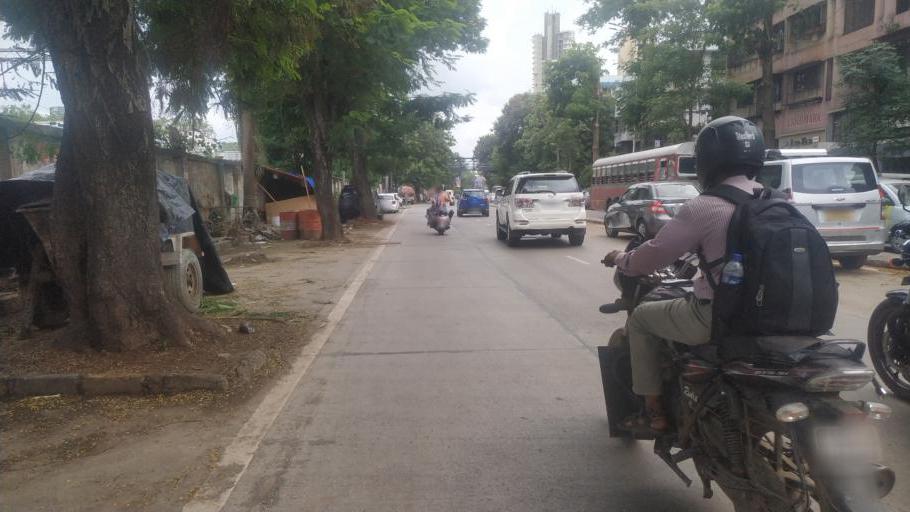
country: IN
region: Maharashtra
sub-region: Mumbai Suburban
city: Mumbai
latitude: 19.0360
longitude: 72.8478
